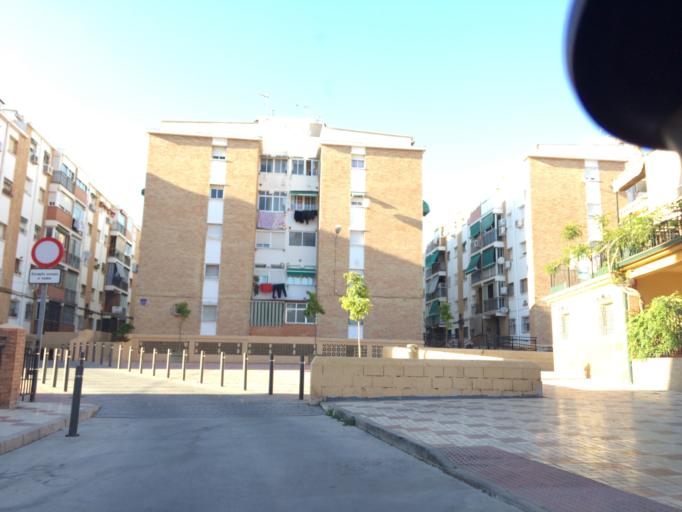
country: ES
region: Andalusia
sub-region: Provincia de Malaga
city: Malaga
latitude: 36.7252
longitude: -4.4494
